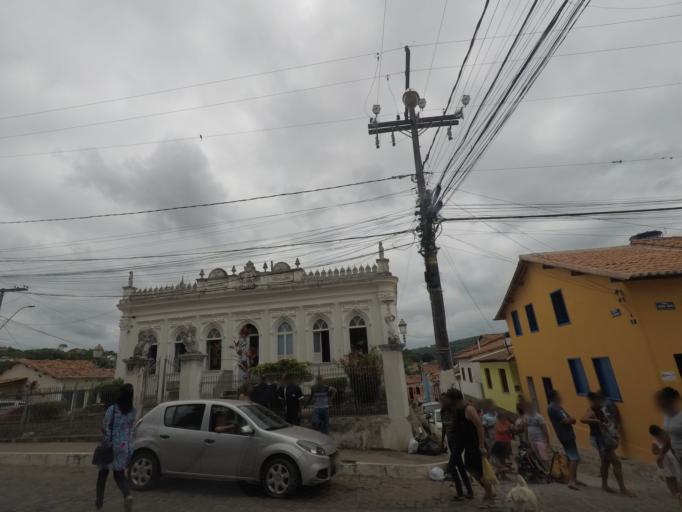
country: BR
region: Bahia
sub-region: Andarai
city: Vera Cruz
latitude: -12.5631
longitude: -41.3910
